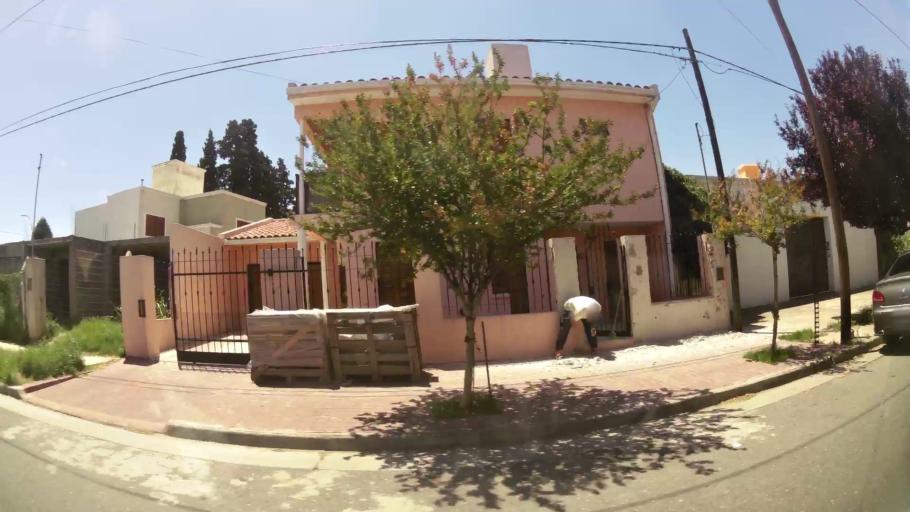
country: AR
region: Cordoba
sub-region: Departamento de Capital
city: Cordoba
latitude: -31.3845
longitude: -64.1424
